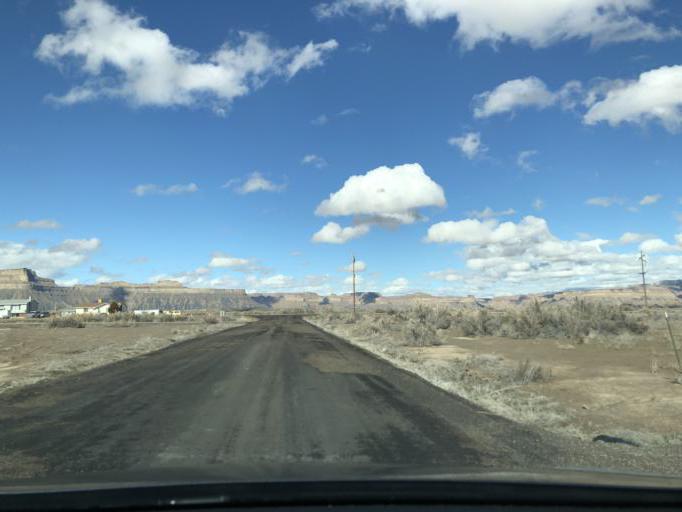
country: US
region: Utah
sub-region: Carbon County
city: East Carbon City
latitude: 38.9992
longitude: -110.1699
